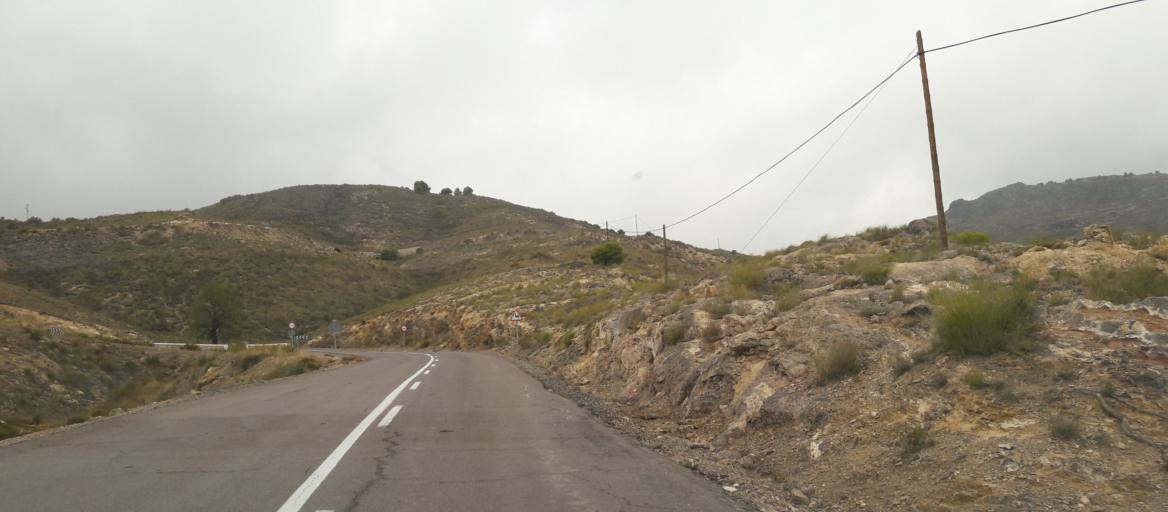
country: ES
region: Andalusia
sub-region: Provincia de Almeria
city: Enix
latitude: 36.8718
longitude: -2.6210
